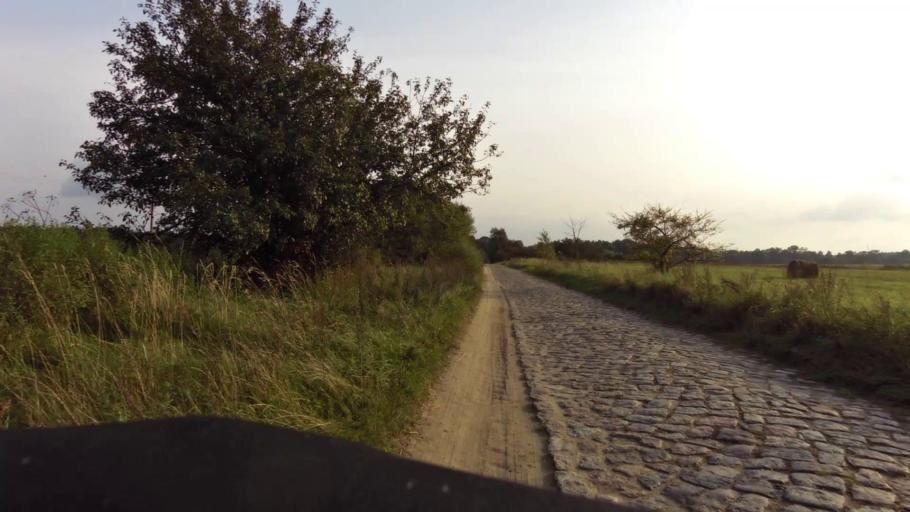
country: PL
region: West Pomeranian Voivodeship
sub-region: Powiat stargardzki
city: Dobrzany
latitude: 53.3364
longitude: 15.3645
